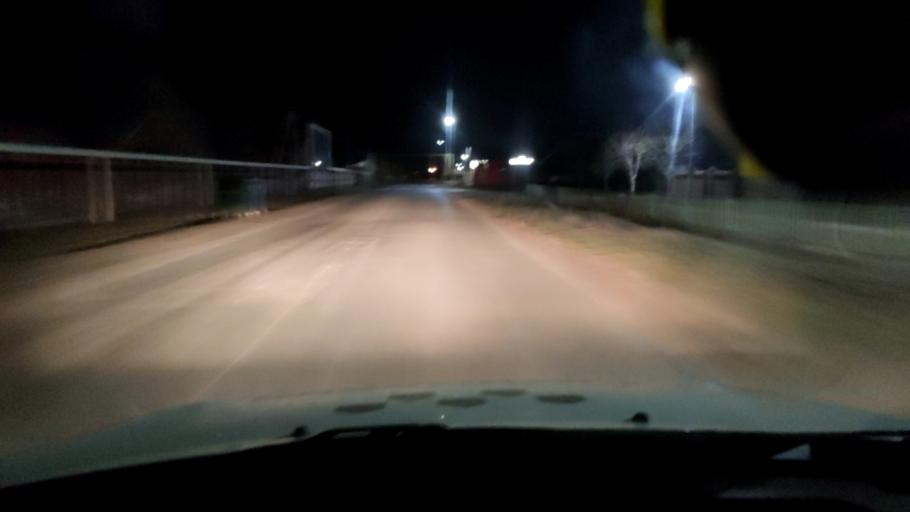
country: RU
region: Samara
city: Podstepki
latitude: 53.6208
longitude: 49.0468
